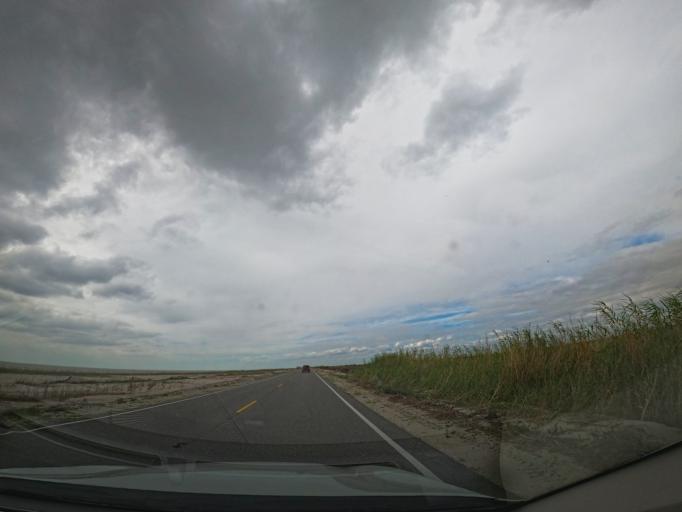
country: US
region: Louisiana
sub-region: Cameron Parish
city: Cameron
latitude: 29.7679
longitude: -93.4007
